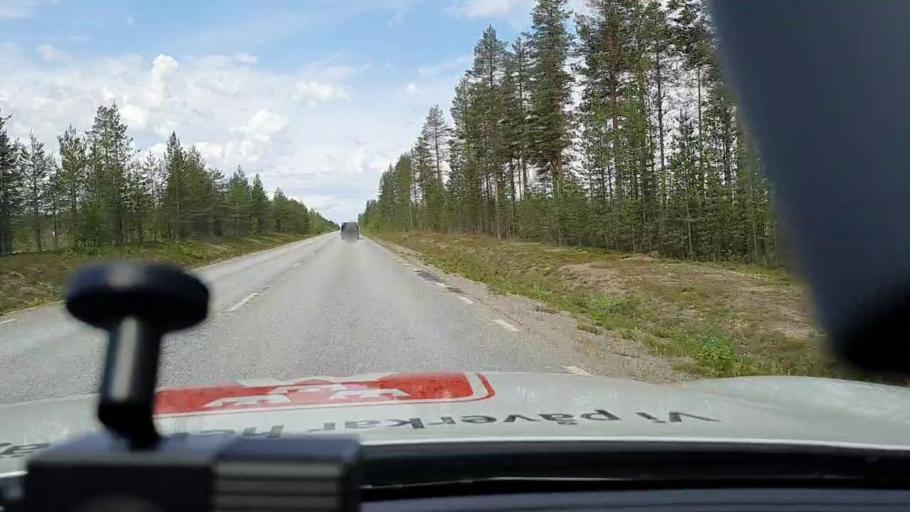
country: SE
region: Norrbotten
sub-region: Jokkmokks Kommun
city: Jokkmokk
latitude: 66.5206
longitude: 20.2144
